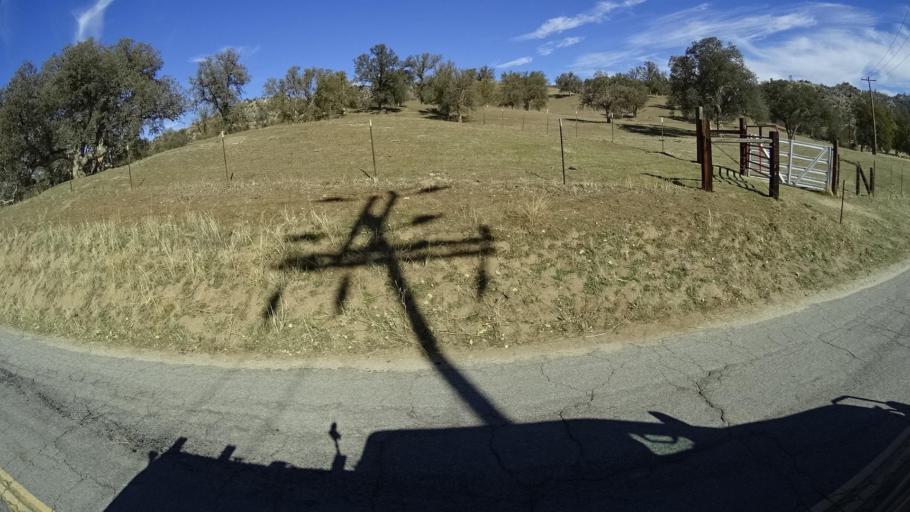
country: US
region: California
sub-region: Kern County
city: Alta Sierra
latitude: 35.6184
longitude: -118.7305
